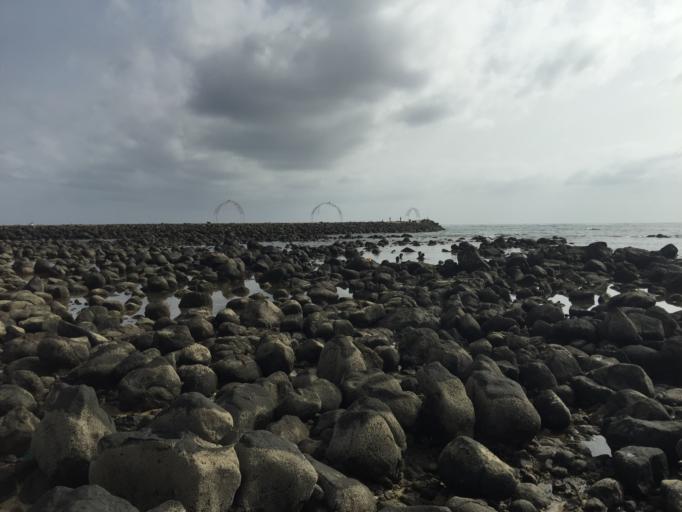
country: SN
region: Dakar
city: Mermoz Boabab
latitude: 14.7447
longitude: -17.5288
